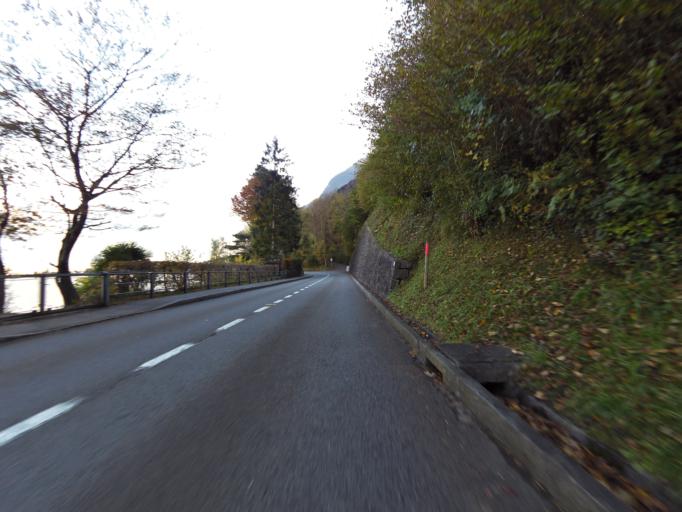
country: CH
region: Uri
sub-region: Uri
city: Flueelen
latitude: 46.8933
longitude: 8.5954
